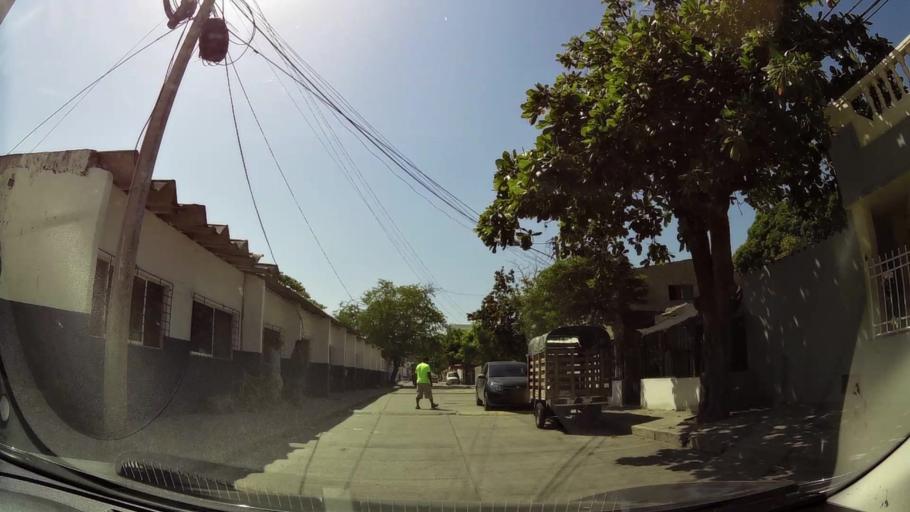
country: CO
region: Bolivar
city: Cartagena
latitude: 10.4412
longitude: -75.5248
